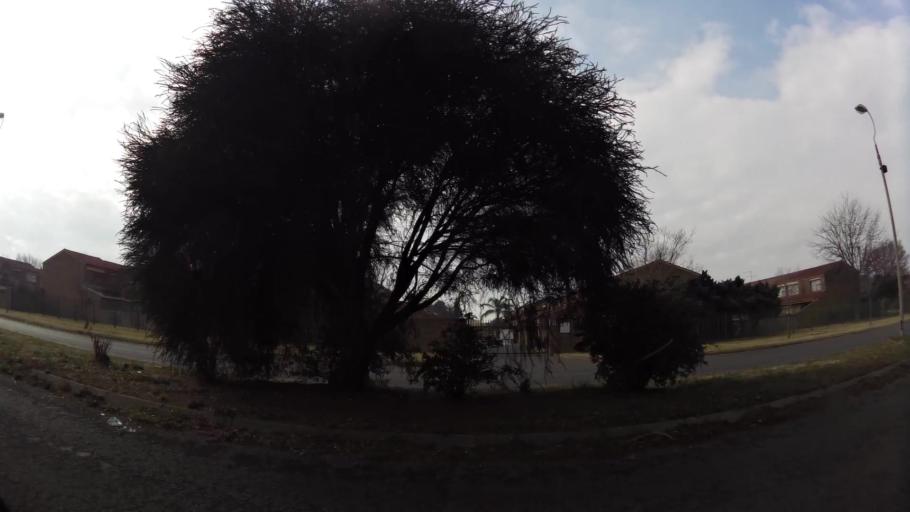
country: ZA
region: Gauteng
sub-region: Sedibeng District Municipality
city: Vanderbijlpark
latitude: -26.6935
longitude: 27.8473
